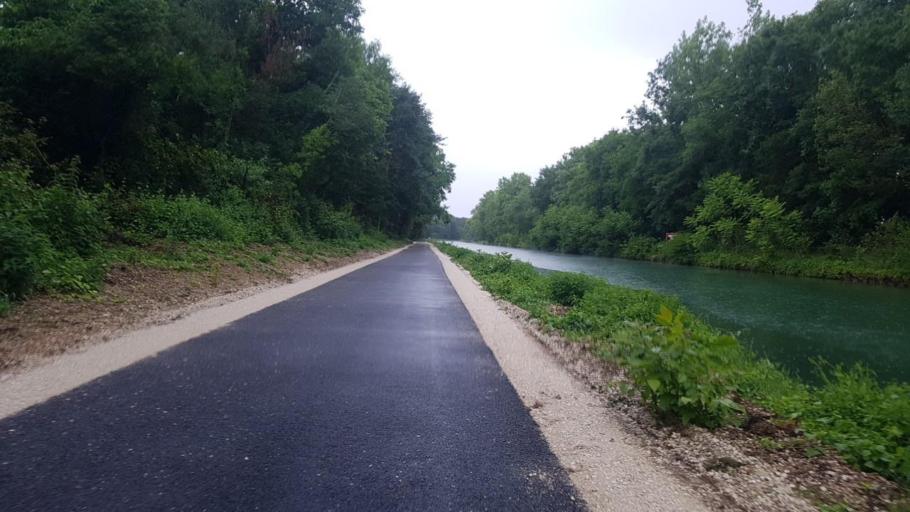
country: FR
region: Champagne-Ardenne
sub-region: Departement de la Marne
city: Sarry
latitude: 48.8677
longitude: 4.4625
